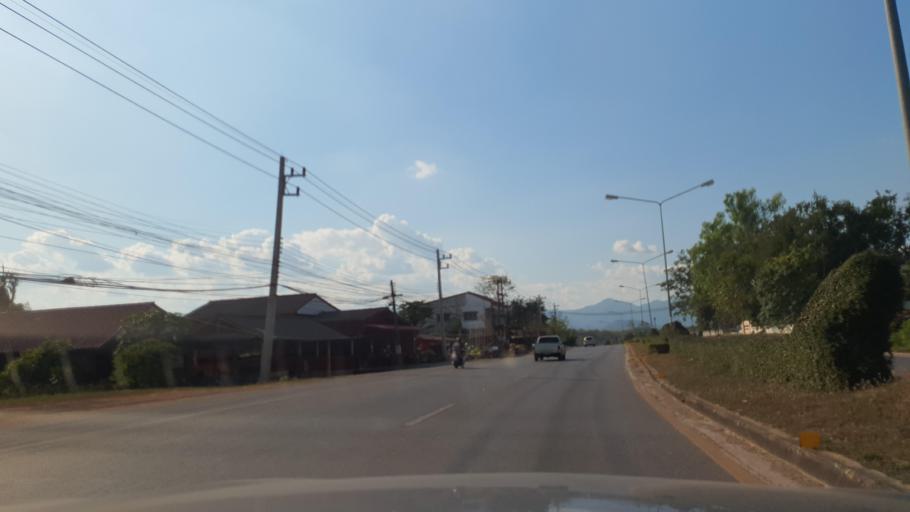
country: TH
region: Nan
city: Nan
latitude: 18.7965
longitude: 100.7207
